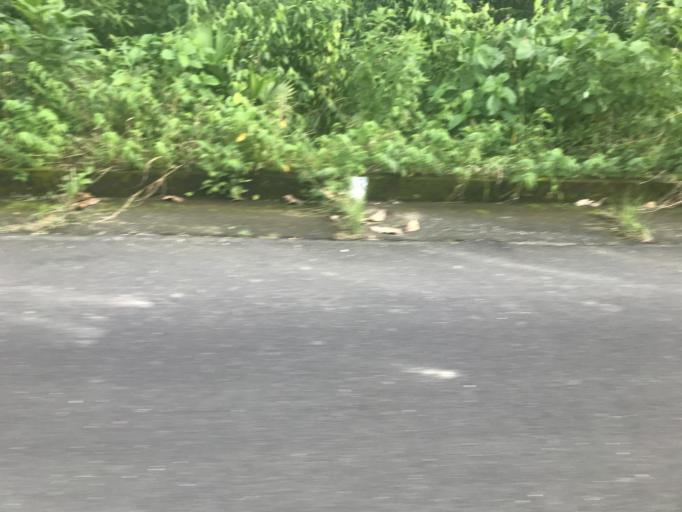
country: EC
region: Napo
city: Tena
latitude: -1.0420
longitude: -77.8027
